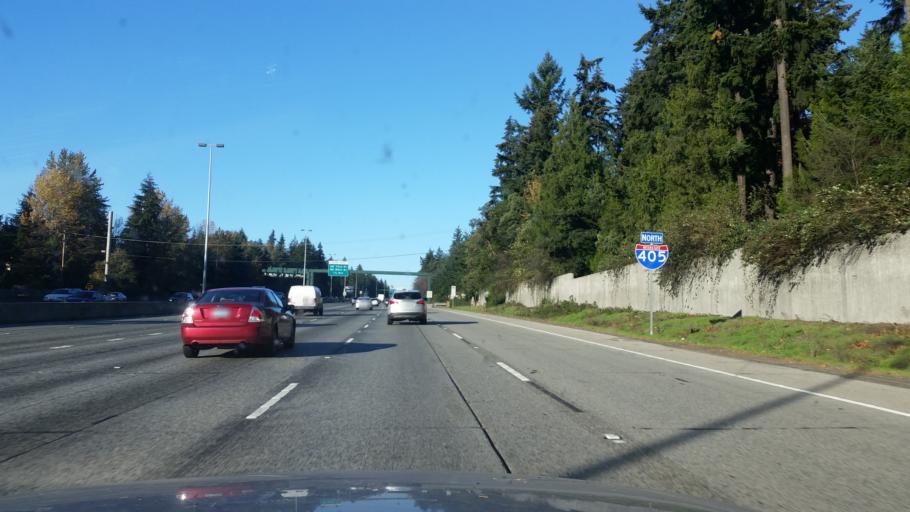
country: US
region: Washington
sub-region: King County
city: Yarrow Point
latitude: 47.6416
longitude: -122.1863
